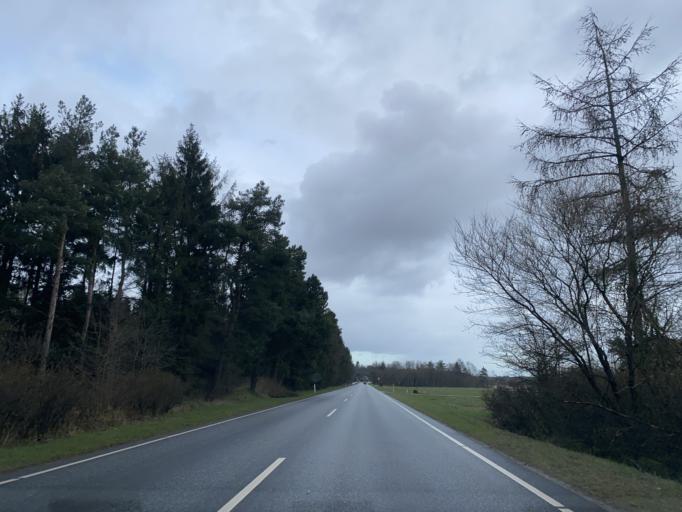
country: DK
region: Central Jutland
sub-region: Viborg Kommune
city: Bjerringbro
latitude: 56.2922
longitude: 9.6583
